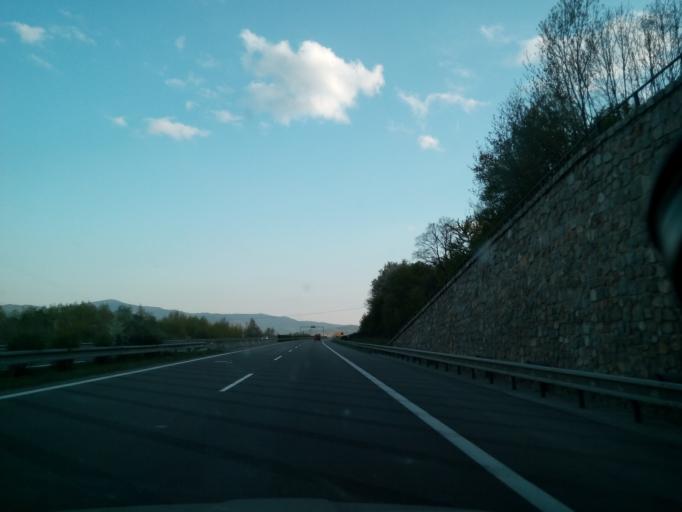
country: SK
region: Trenciansky
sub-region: Okres Trencin
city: Trencin
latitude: 48.8885
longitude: 17.9814
